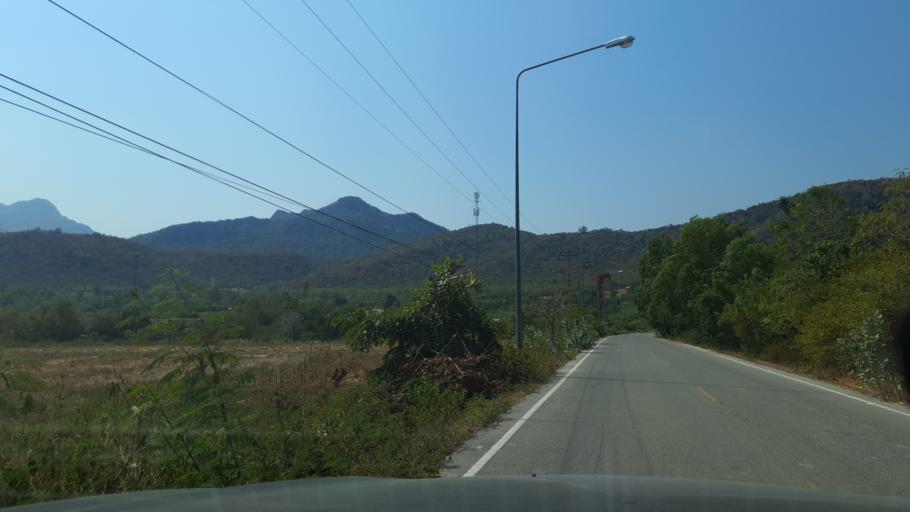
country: TH
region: Prachuap Khiri Khan
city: Sam Roi Yot
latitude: 12.2857
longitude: 99.9695
